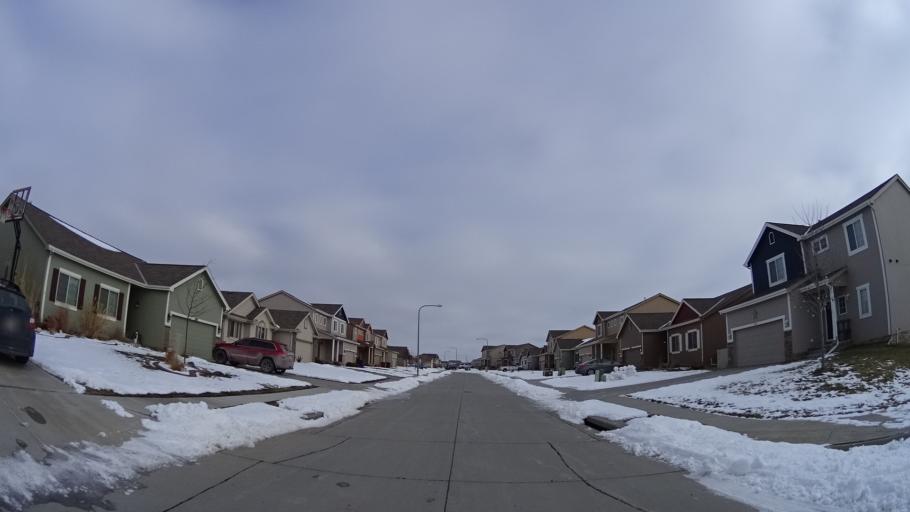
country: US
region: Nebraska
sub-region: Sarpy County
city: Offutt Air Force Base
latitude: 41.1040
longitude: -95.9833
